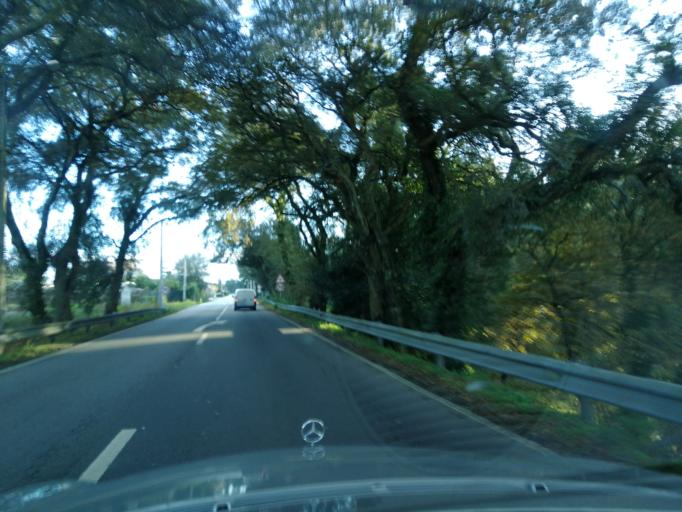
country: PT
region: Braga
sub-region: Esposende
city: Marinhas
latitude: 41.5973
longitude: -8.7389
